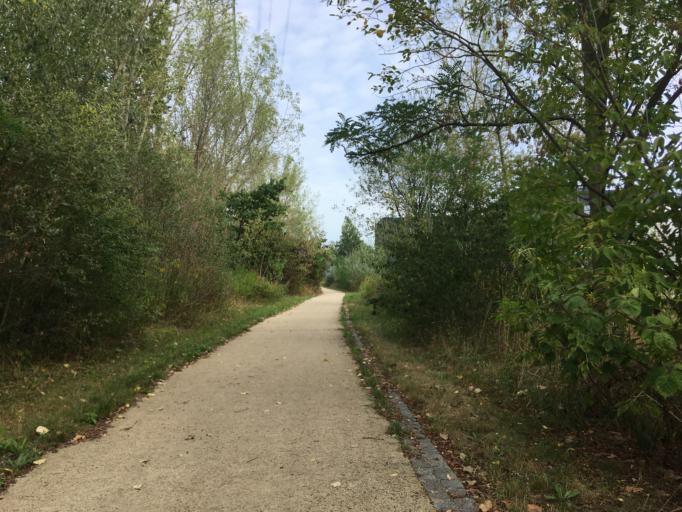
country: DE
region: Berlin
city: Falkenberg
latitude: 52.5577
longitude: 13.5437
